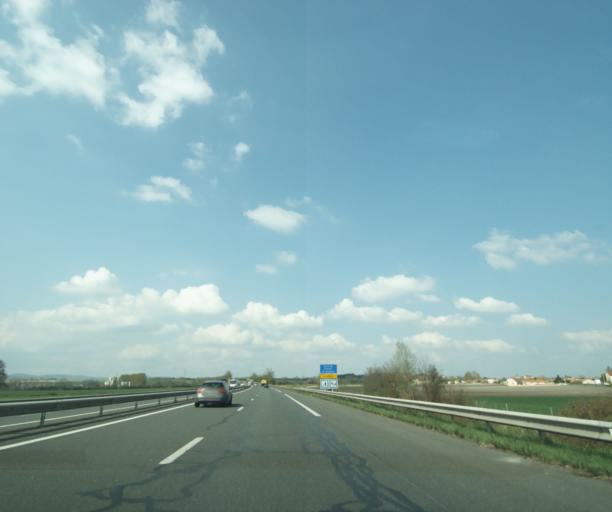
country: FR
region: Auvergne
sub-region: Departement du Puy-de-Dome
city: Riom
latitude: 45.9099
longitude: 3.1536
